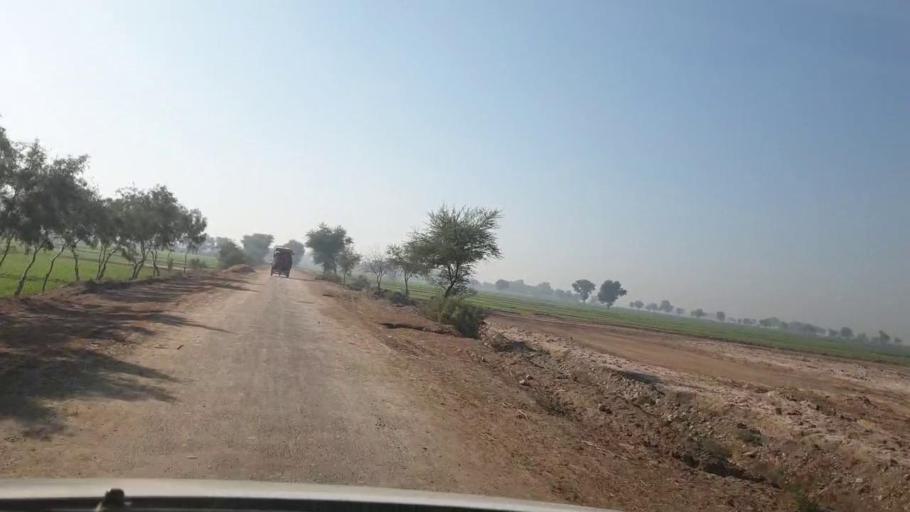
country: PK
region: Sindh
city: Dadu
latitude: 26.6461
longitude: 67.8218
